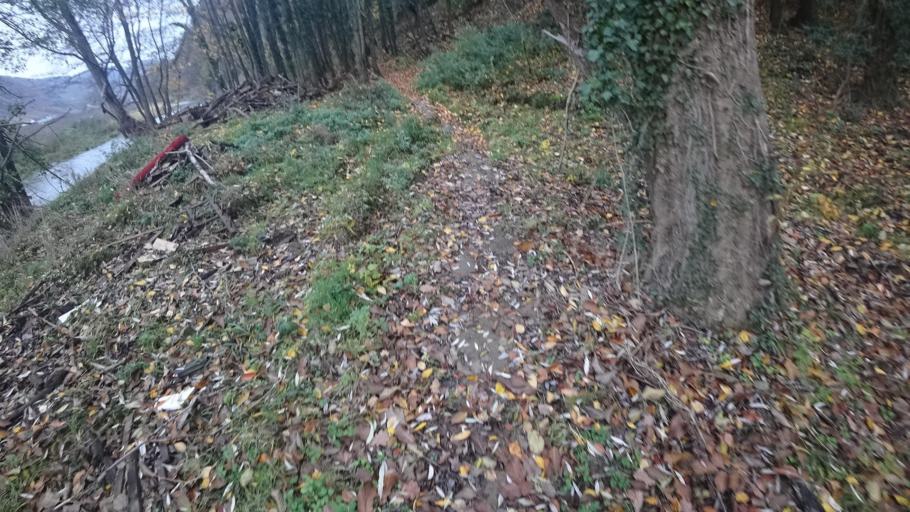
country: DE
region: Rheinland-Pfalz
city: Rech
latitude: 50.5208
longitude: 7.0425
